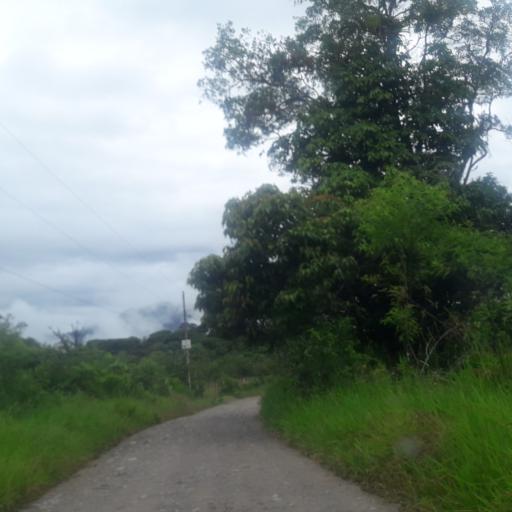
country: EC
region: Napo
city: Archidona
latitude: -0.9177
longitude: -77.8199
